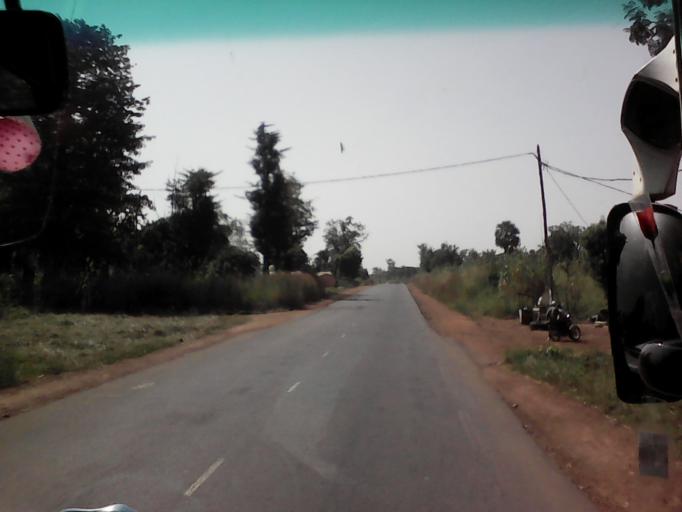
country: TG
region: Centrale
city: Sotouboua
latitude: 8.6934
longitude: 1.0235
